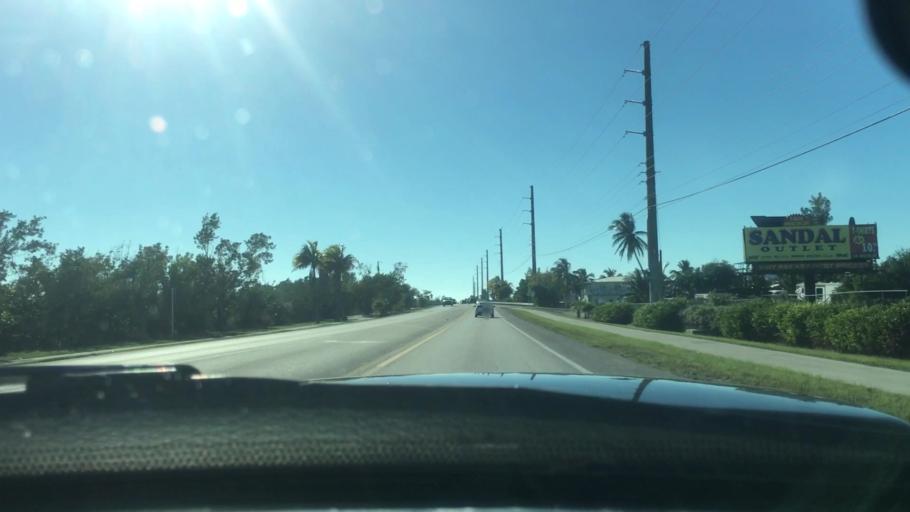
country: US
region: Florida
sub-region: Monroe County
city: Big Coppitt Key
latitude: 24.5944
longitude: -81.6627
